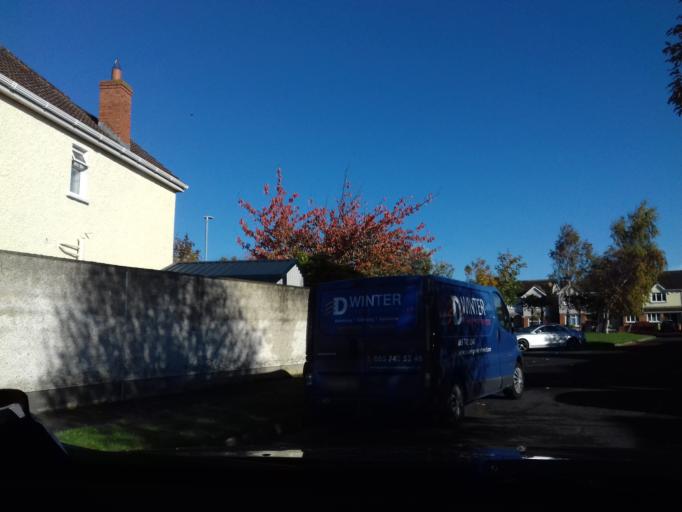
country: IE
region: Leinster
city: Cabra
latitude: 53.3616
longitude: -6.3039
